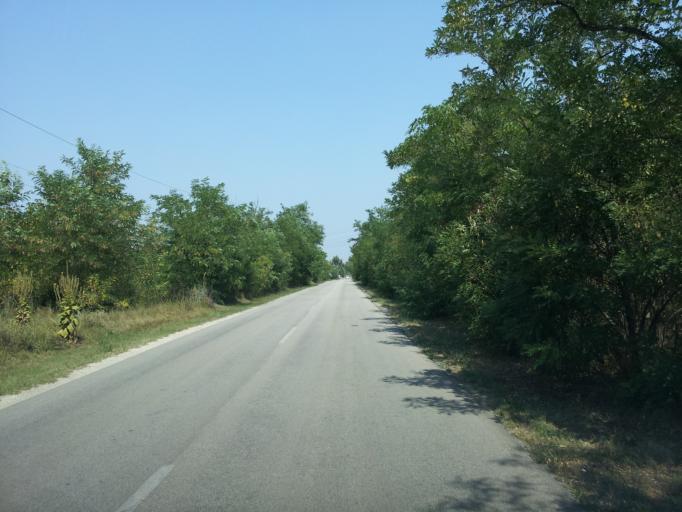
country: HU
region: Pest
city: Dunavarsany
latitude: 47.2665
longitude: 19.0636
